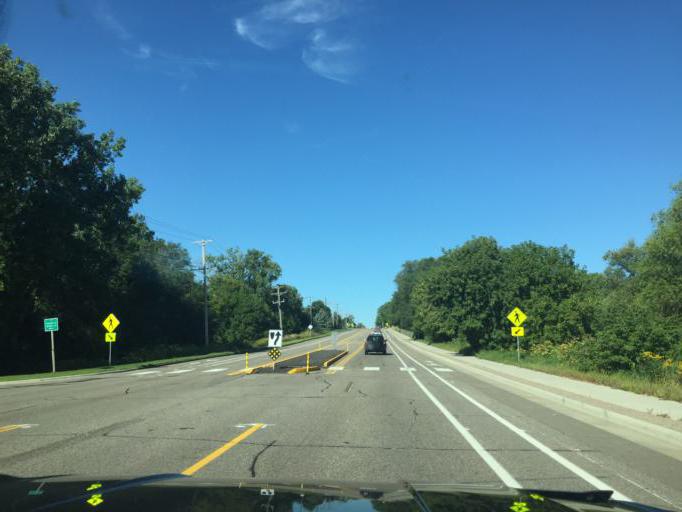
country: US
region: Minnesota
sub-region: Ramsey County
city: Roseville
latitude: 44.9918
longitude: -93.1170
